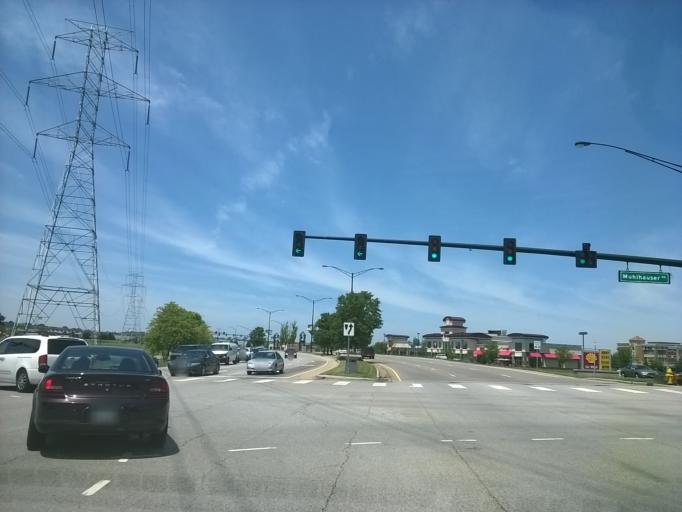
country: US
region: Ohio
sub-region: Butler County
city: Beckett Ridge
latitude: 39.3239
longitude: -84.4276
